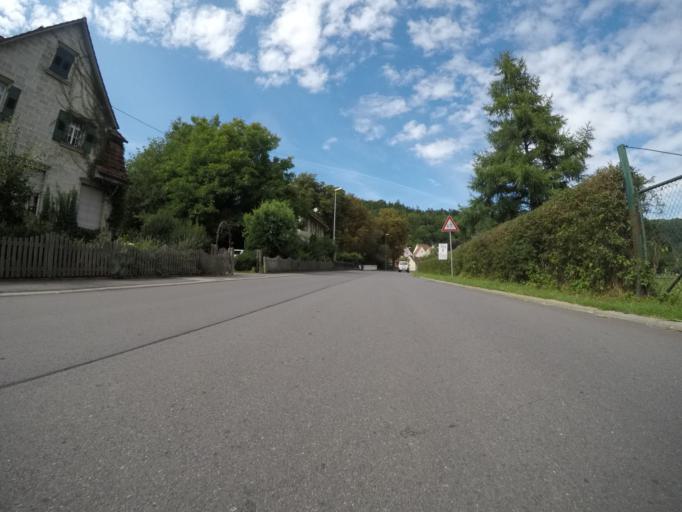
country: DE
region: Baden-Wuerttemberg
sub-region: Tuebingen Region
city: Hirrlingen
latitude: 48.4569
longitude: 8.8705
